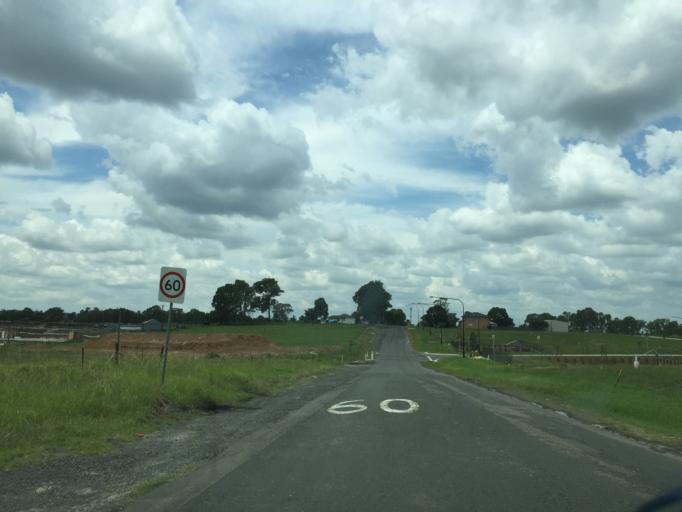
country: AU
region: New South Wales
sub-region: Blacktown
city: Riverstone
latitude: -33.6977
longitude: 150.8874
